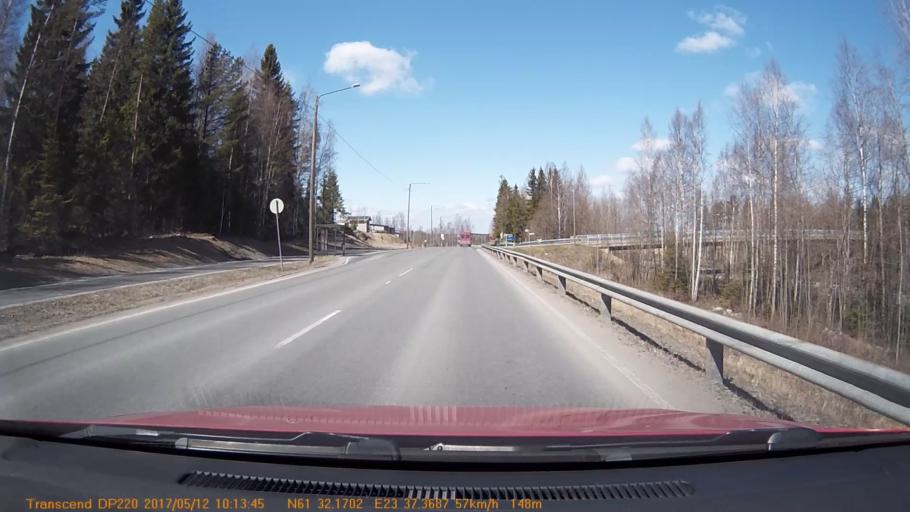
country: FI
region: Pirkanmaa
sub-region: Tampere
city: Yloejaervi
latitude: 61.5359
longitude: 23.6232
